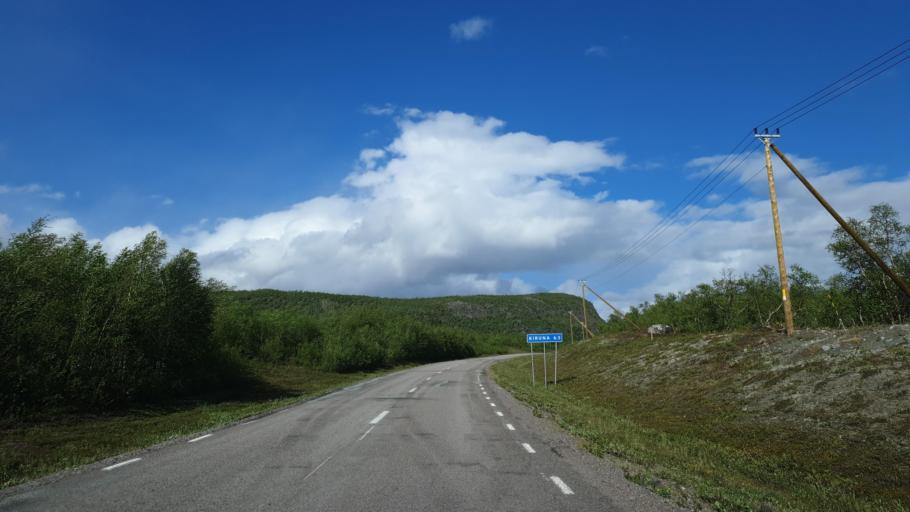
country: SE
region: Norrbotten
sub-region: Kiruna Kommun
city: Kiruna
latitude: 67.8629
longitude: 19.0362
